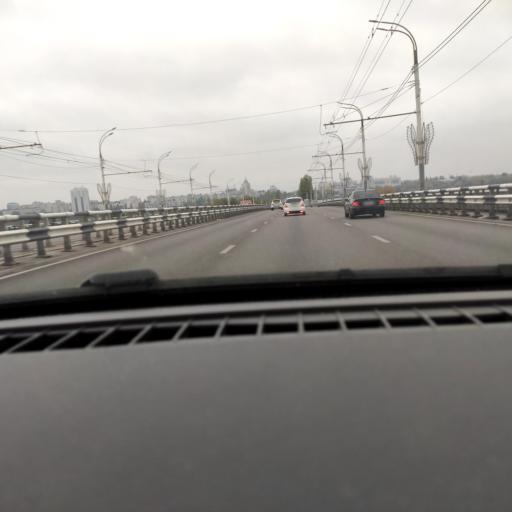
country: RU
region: Voronezj
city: Voronezh
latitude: 51.6659
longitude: 39.2241
